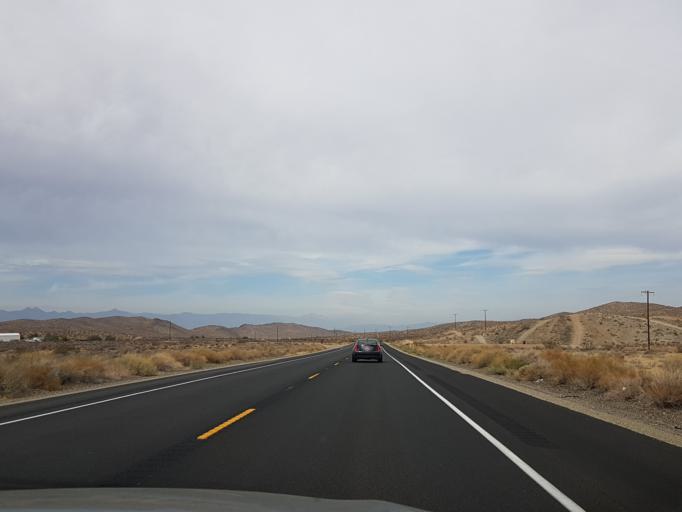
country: US
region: California
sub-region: Kern County
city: Ridgecrest
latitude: 35.5181
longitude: -117.6723
